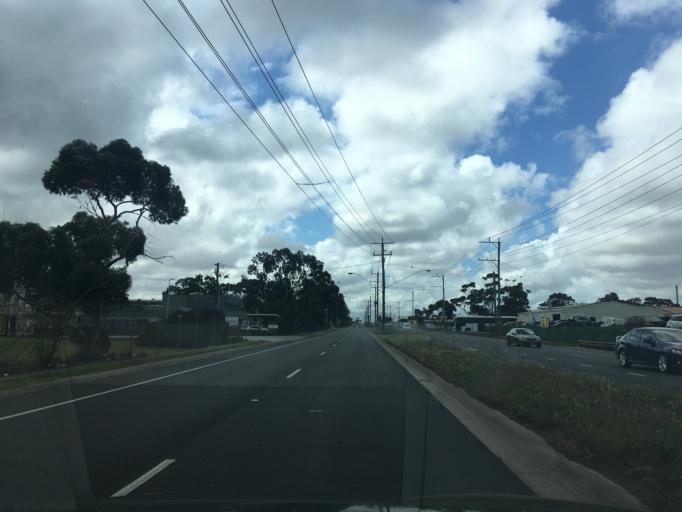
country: AU
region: Victoria
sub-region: Hobsons Bay
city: Laverton
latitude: -37.8376
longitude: 144.7834
